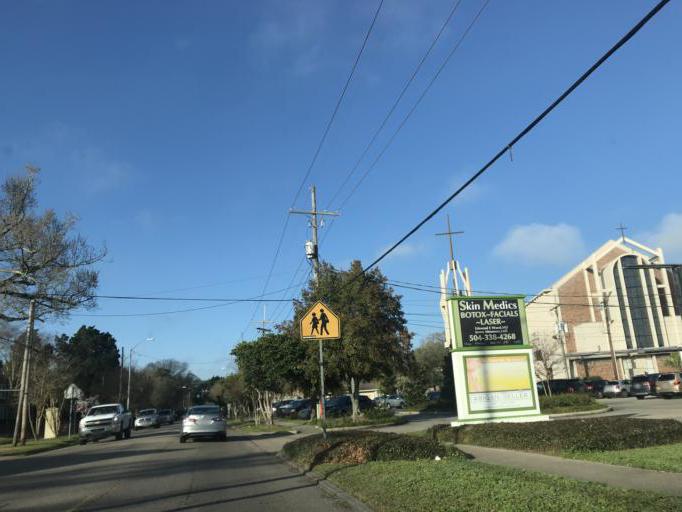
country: US
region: Louisiana
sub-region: Jefferson Parish
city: Metairie
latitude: 29.9863
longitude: -90.1419
